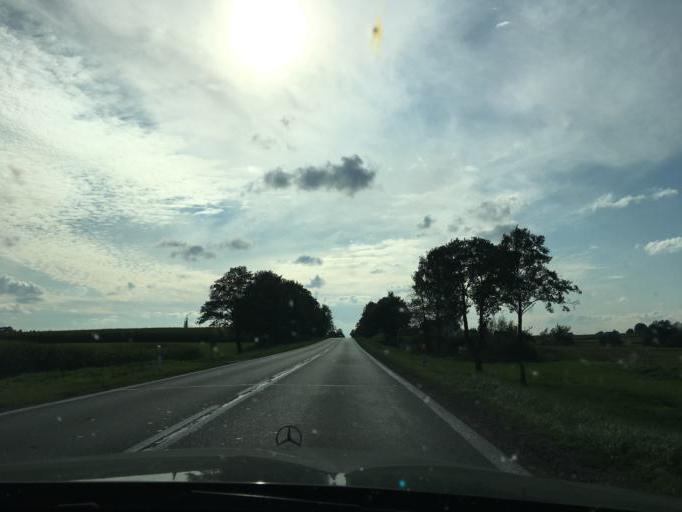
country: PL
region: Podlasie
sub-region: Powiat augustowski
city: Augustow
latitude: 53.8200
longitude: 22.9327
